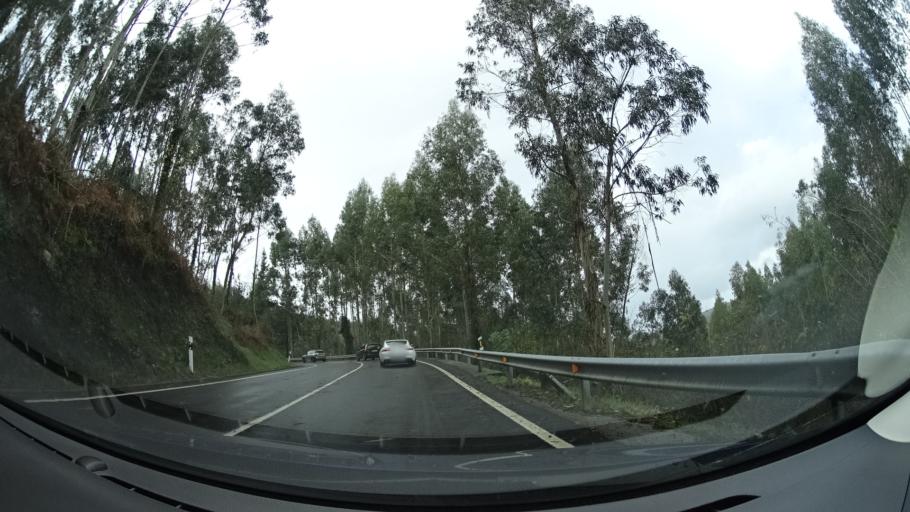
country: ES
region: Basque Country
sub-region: Bizkaia
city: Bakio
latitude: 43.3849
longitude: -2.7722
